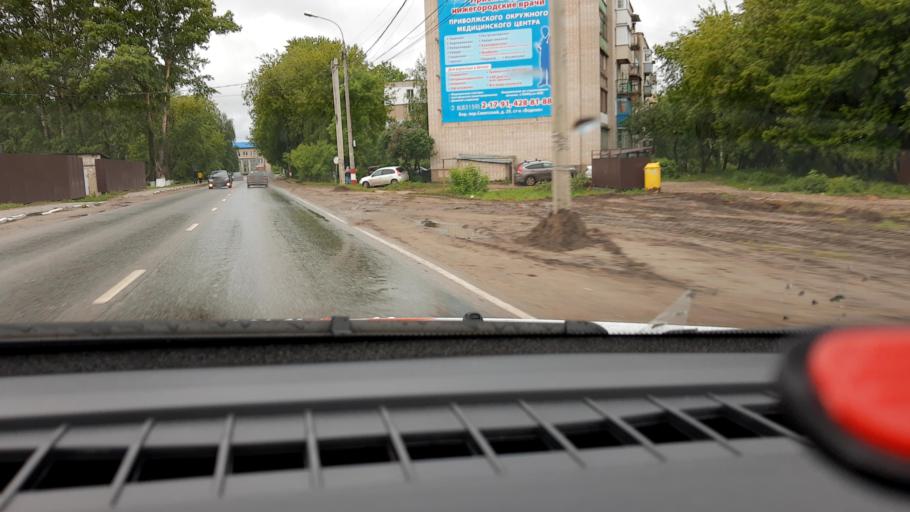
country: RU
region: Nizjnij Novgorod
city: Bor
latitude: 56.3609
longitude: 44.0666
